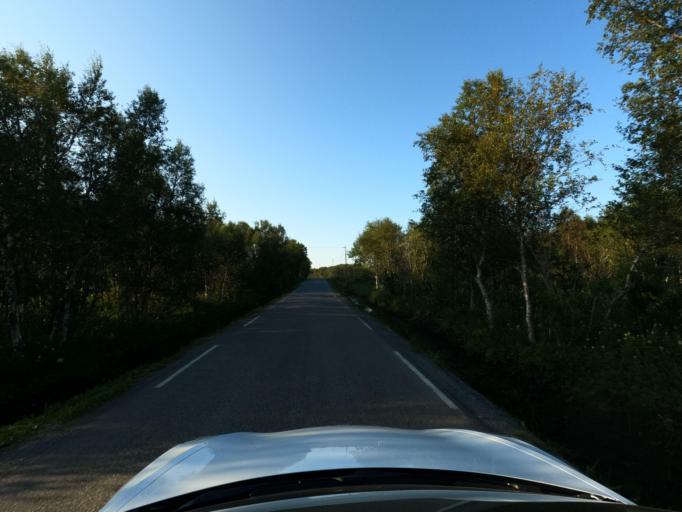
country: NO
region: Troms
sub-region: Skanland
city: Evenskjer
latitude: 68.4712
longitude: 16.7039
